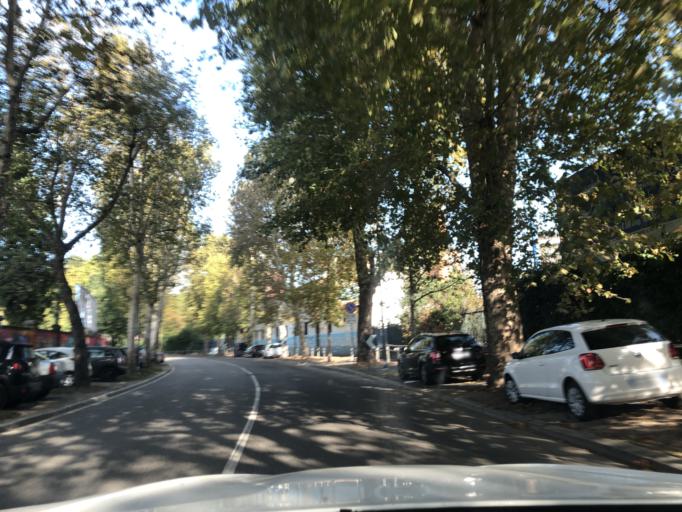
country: IT
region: Lombardy
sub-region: Citta metropolitana di Milano
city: Novate Milanese
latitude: 45.4815
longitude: 9.1405
